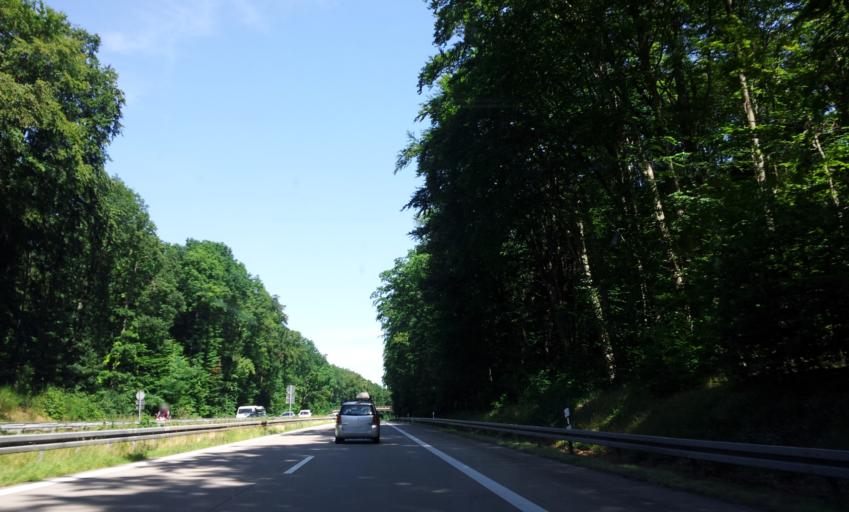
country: DE
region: Brandenburg
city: Gramzow
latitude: 53.1476
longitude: 13.8986
